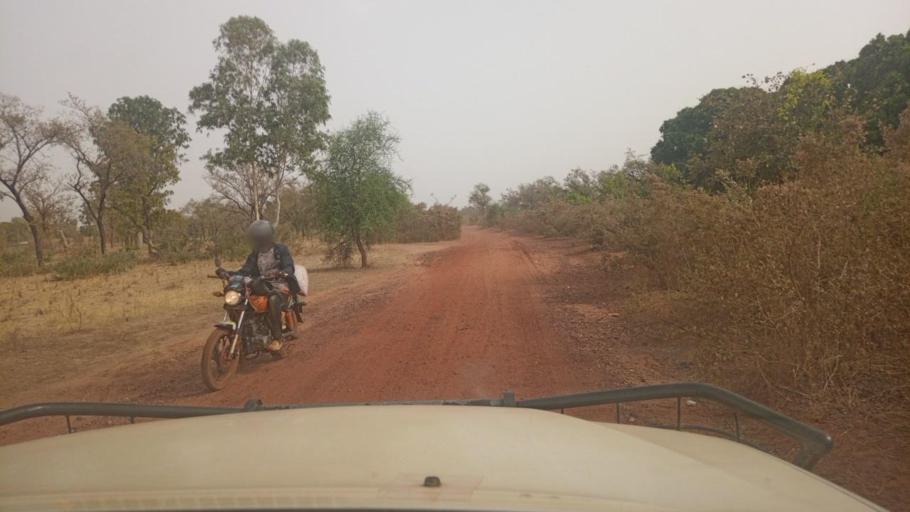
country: BF
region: Boucle du Mouhoun
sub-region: Province des Banwa
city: Salanso
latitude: 12.1092
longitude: -4.3363
